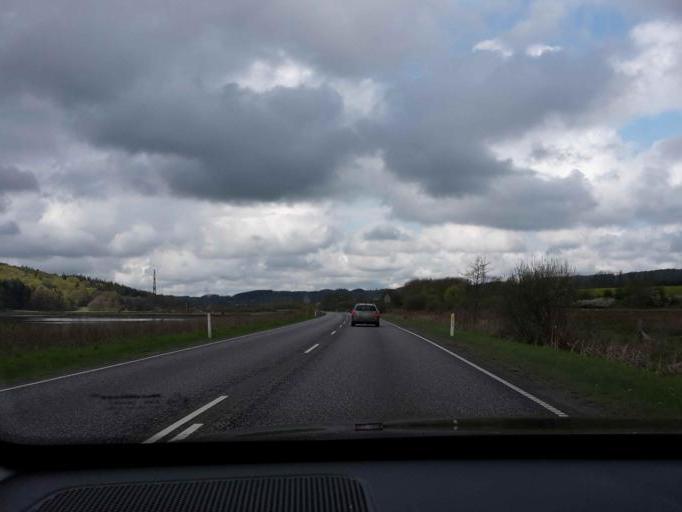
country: DK
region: South Denmark
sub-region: Vejle Kommune
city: Vejle
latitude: 55.7070
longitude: 9.4914
